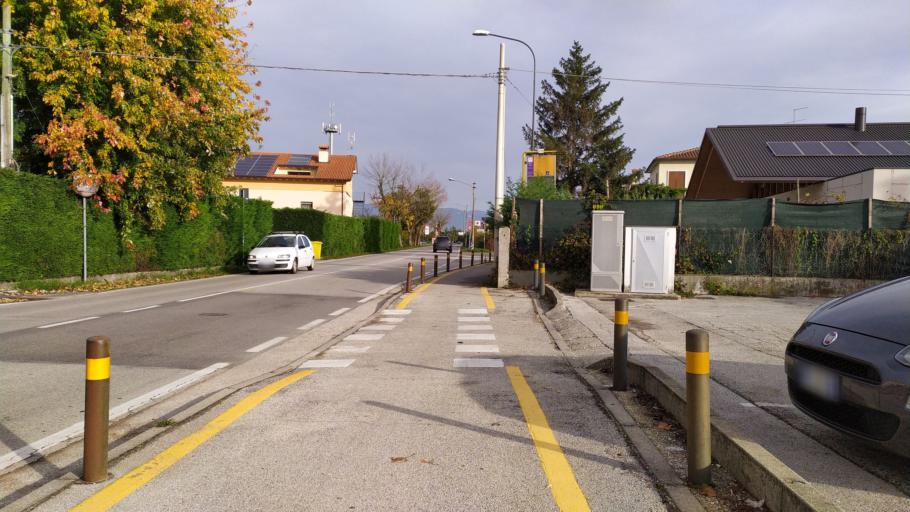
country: IT
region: Veneto
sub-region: Provincia di Vicenza
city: Vicenza
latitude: 45.5724
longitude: 11.5362
